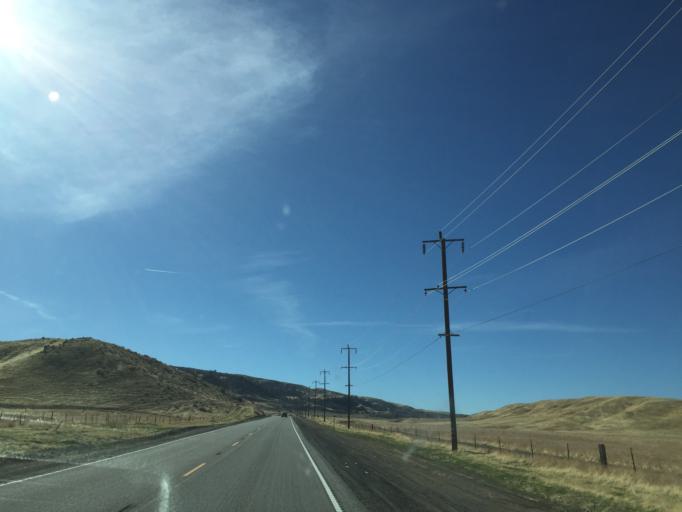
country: US
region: California
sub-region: Kern County
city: Lebec
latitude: 34.7697
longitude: -118.7016
